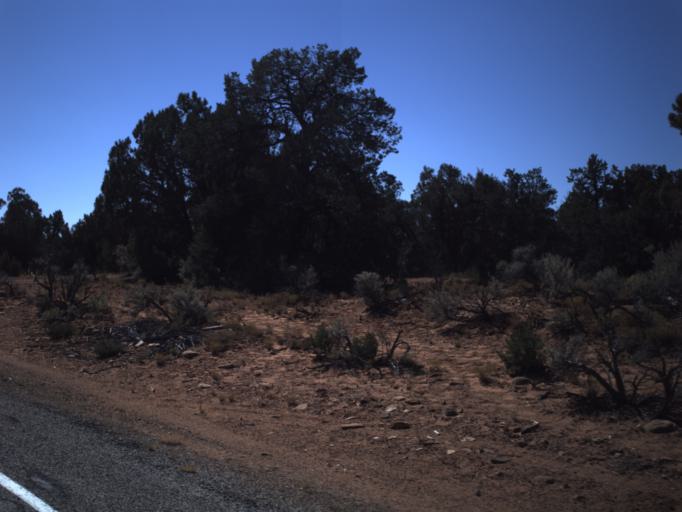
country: US
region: Utah
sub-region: San Juan County
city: Blanding
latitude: 37.5128
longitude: -109.8942
